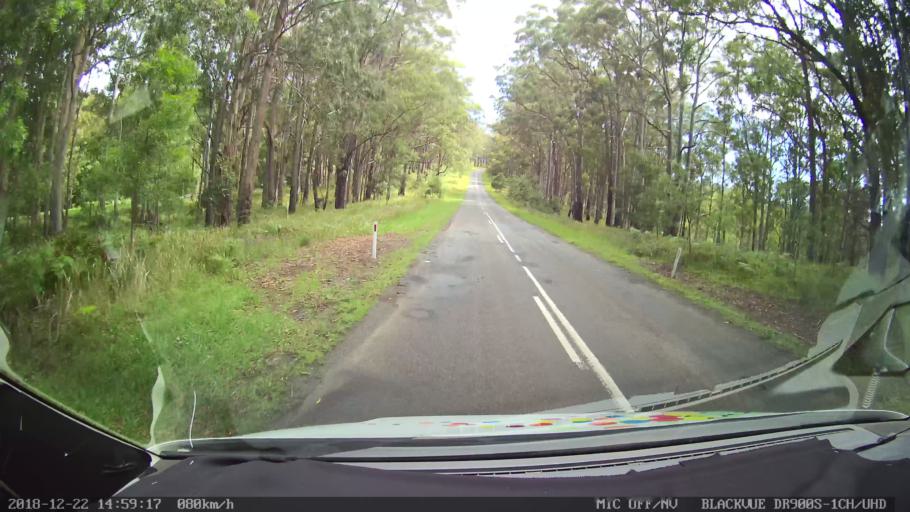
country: AU
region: New South Wales
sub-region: Bellingen
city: Dorrigo
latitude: -30.2455
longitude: 152.4827
